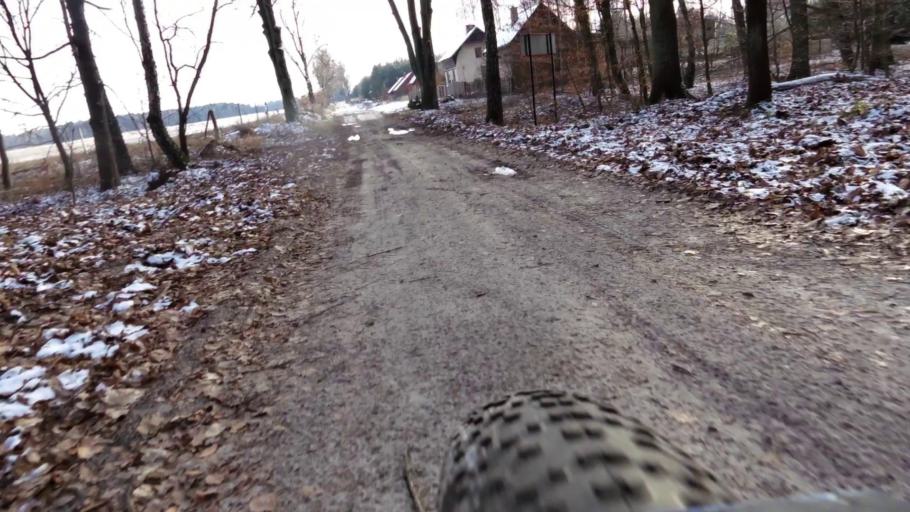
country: PL
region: West Pomeranian Voivodeship
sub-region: Powiat walecki
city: Walcz
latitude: 53.2717
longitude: 16.3087
